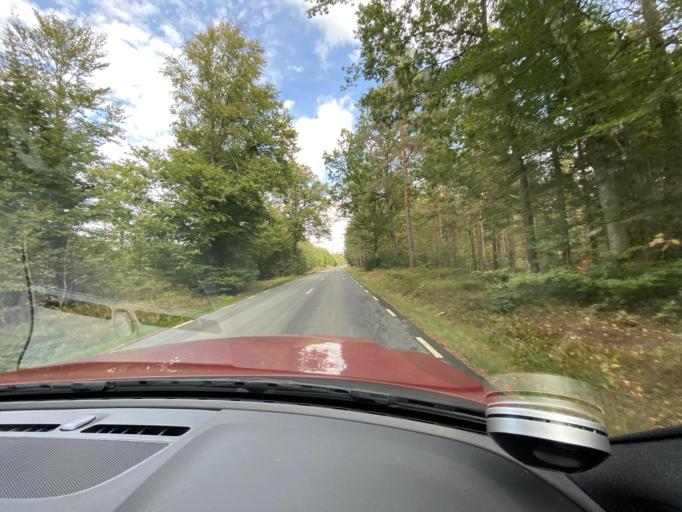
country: SE
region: Skane
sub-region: Hassleholms Kommun
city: Bjarnum
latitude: 56.3367
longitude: 13.6818
